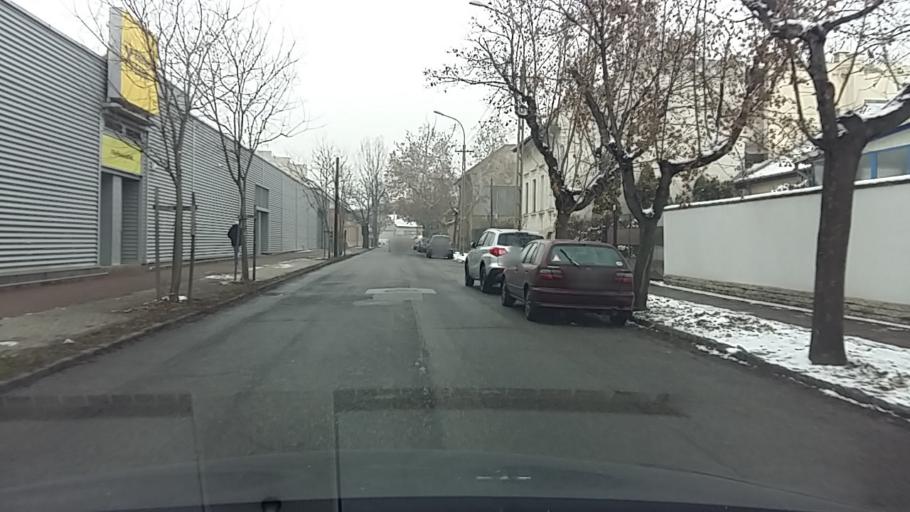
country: HU
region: Budapest
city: Budapest XV. keruelet
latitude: 47.5609
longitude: 19.1072
